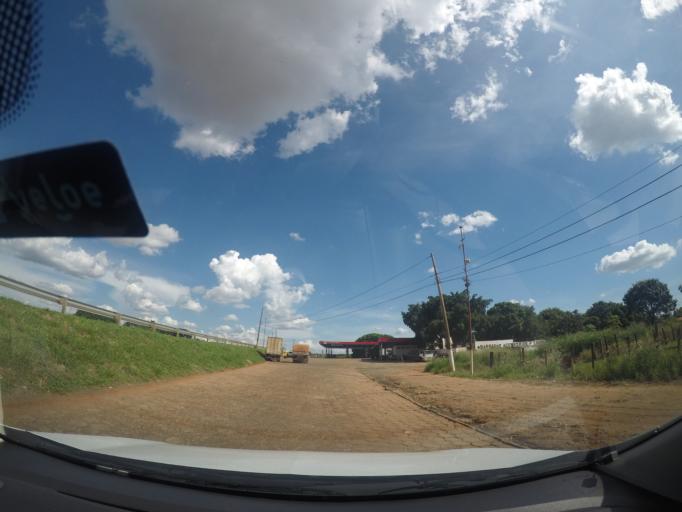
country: BR
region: Sao Paulo
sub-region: Barretos
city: Barretos
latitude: -20.5423
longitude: -48.5947
